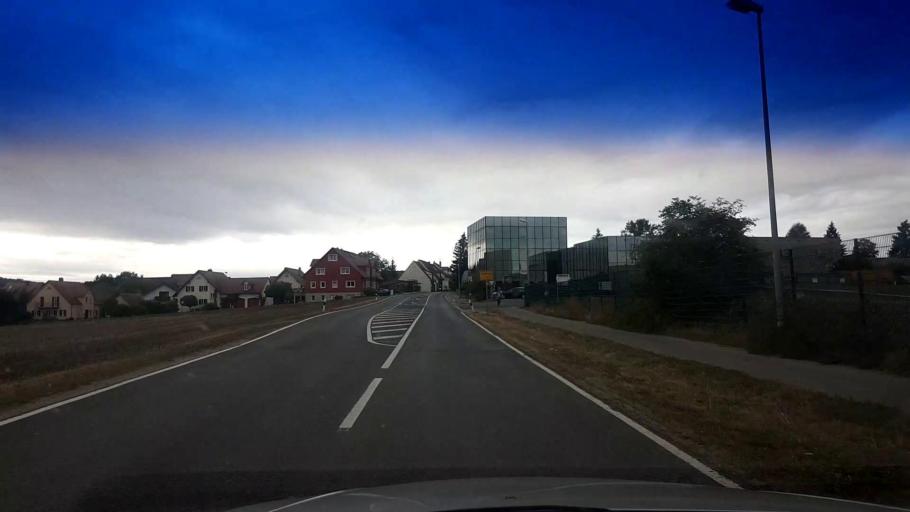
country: DE
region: Bavaria
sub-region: Upper Franconia
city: Stegaurach
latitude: 49.8576
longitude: 10.8614
